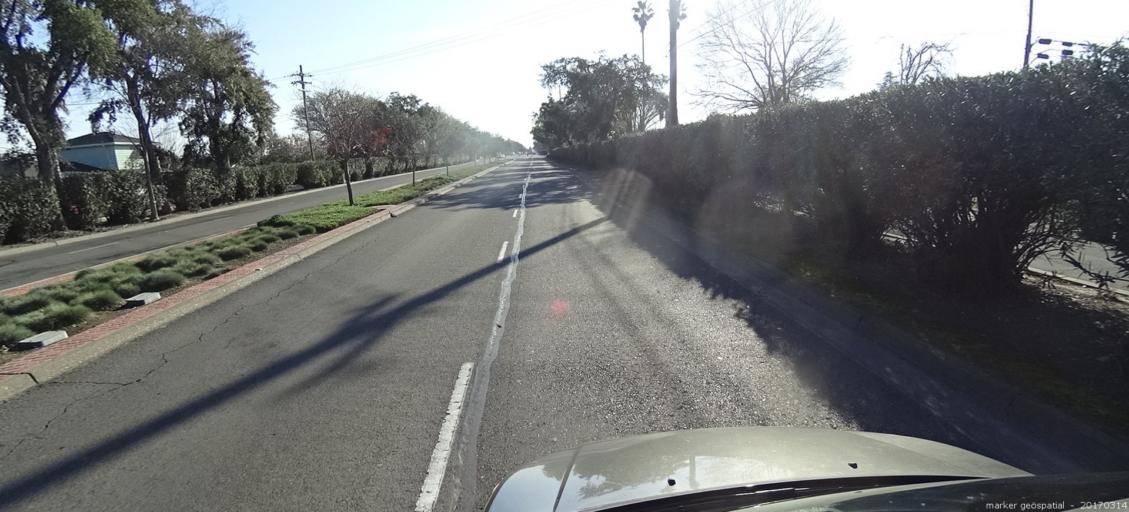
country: US
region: California
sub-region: Sacramento County
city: Parkway
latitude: 38.4956
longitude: -121.5021
